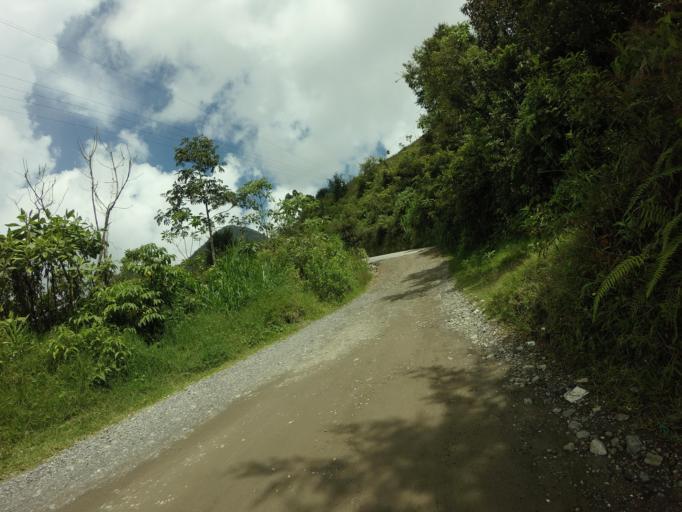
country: CO
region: Caldas
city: Manzanares
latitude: 5.2677
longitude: -75.1403
